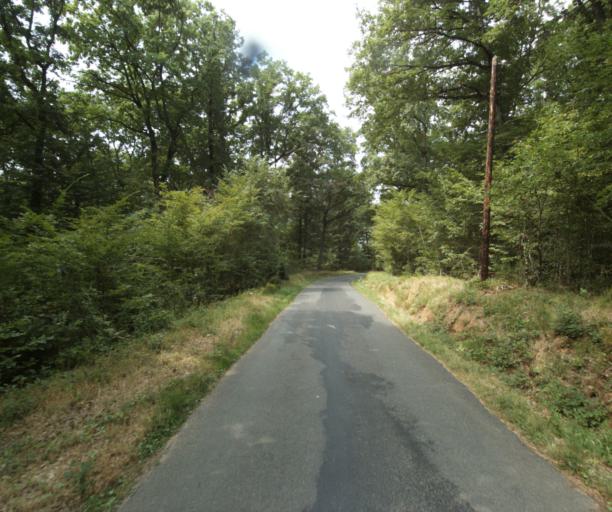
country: FR
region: Bourgogne
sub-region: Departement de Saone-et-Loire
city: Gueugnon
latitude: 46.5886
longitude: 4.0789
